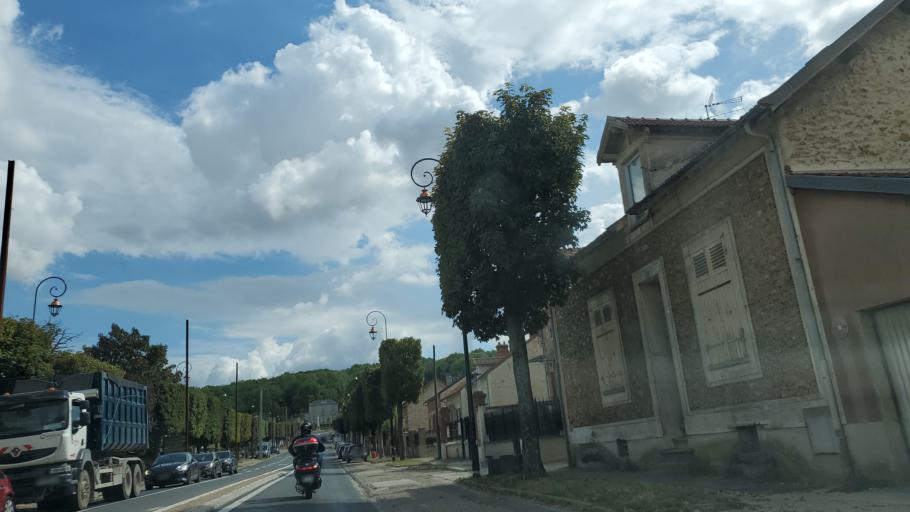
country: FR
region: Ile-de-France
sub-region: Departement de Seine-et-Marne
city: Coulommiers
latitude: 48.8030
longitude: 3.0857
